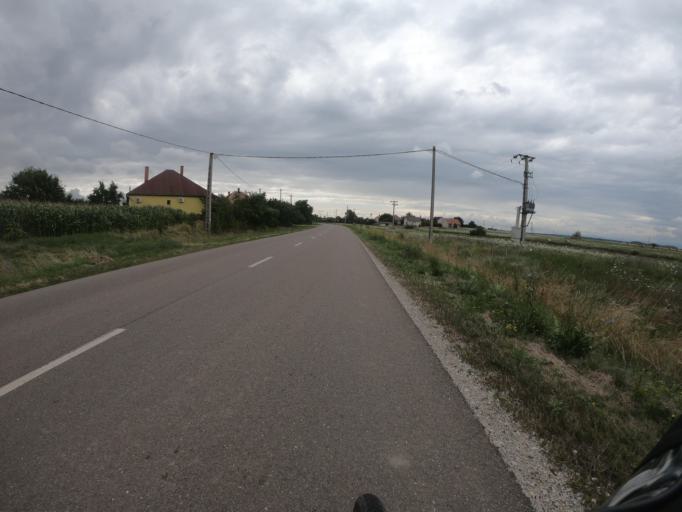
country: HU
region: Jasz-Nagykun-Szolnok
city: Tiszafured
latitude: 47.6907
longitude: 20.7548
